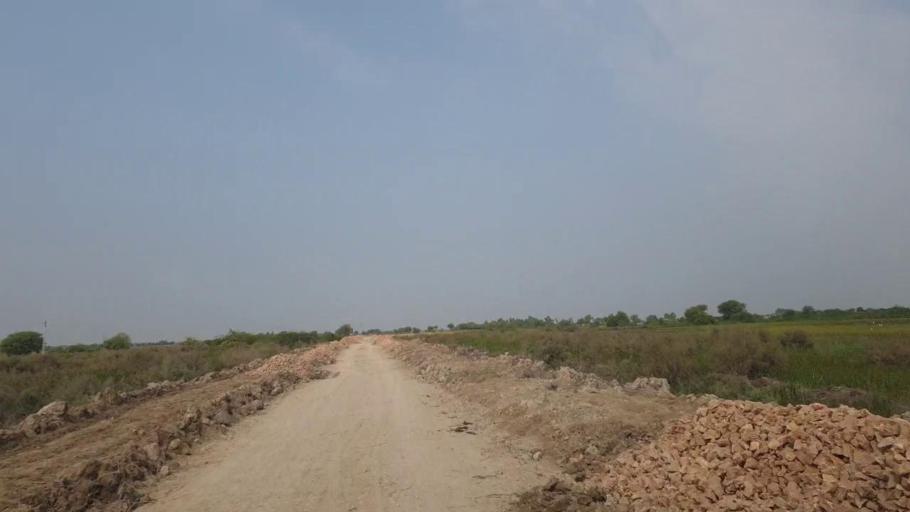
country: PK
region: Sindh
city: Badin
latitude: 24.6092
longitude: 68.7416
